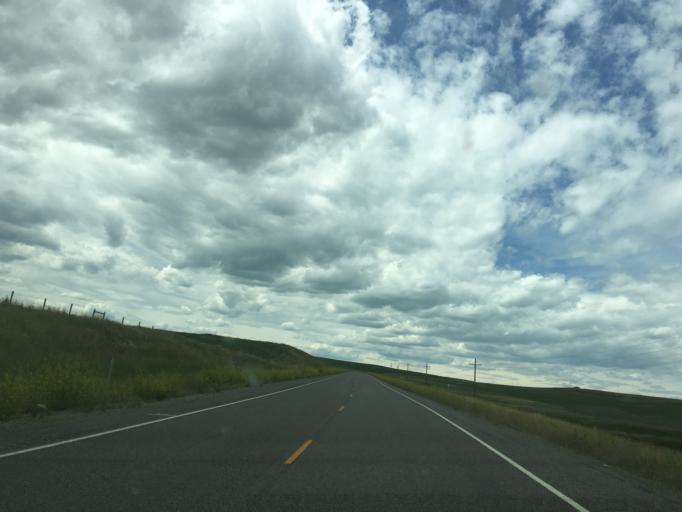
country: US
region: Montana
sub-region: Teton County
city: Choteau
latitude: 48.1370
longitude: -112.3945
